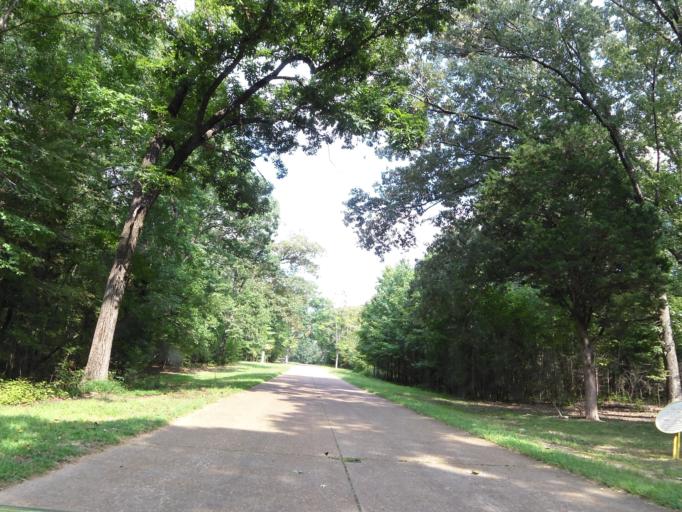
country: US
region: Tennessee
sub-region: Hardin County
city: Crump
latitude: 35.1283
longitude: -88.3322
